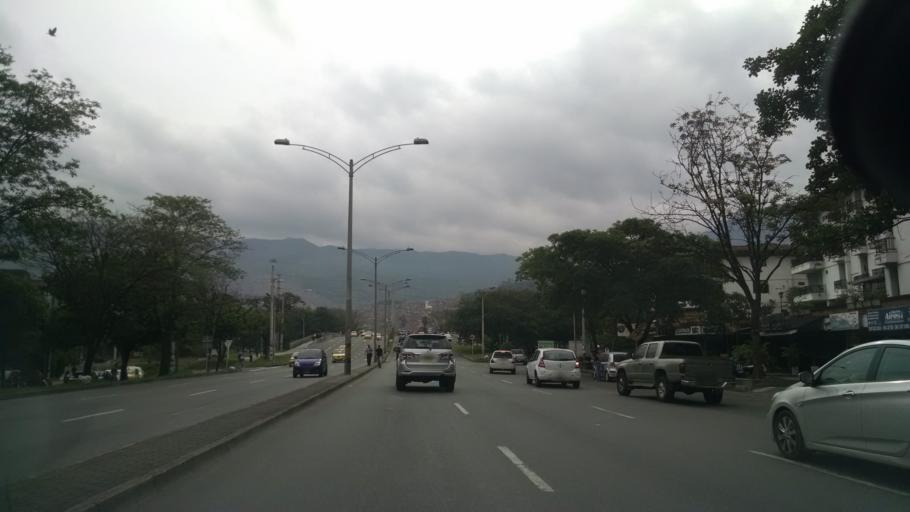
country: CO
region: Antioquia
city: Medellin
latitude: 6.2396
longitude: -75.5795
